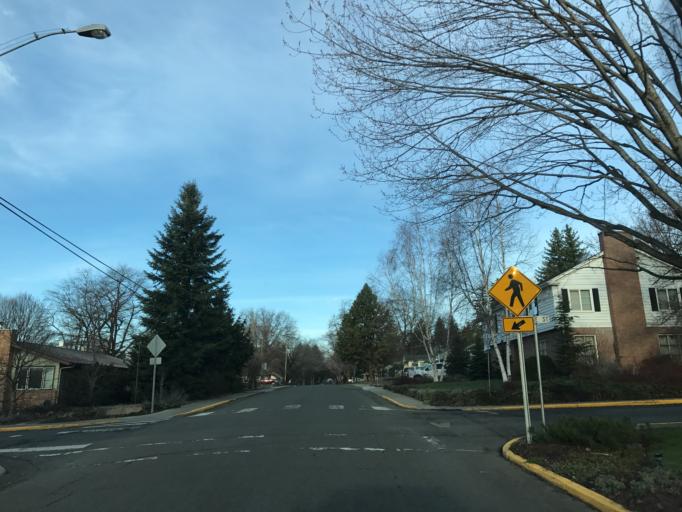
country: US
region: Idaho
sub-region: Latah County
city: Moscow
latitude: 46.7356
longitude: -116.9856
